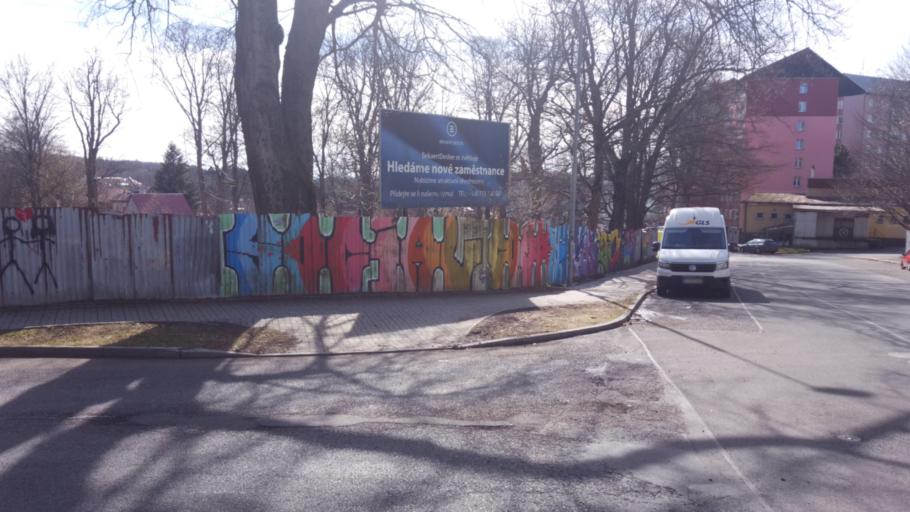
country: CZ
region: Karlovarsky
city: As
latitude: 50.2230
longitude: 12.1990
